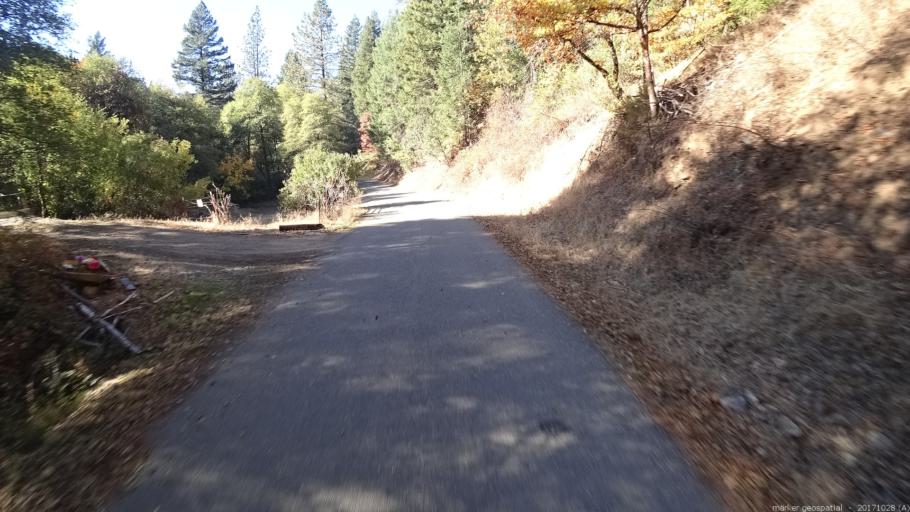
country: US
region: California
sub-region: Shasta County
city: Shasta
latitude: 40.7621
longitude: -122.5684
